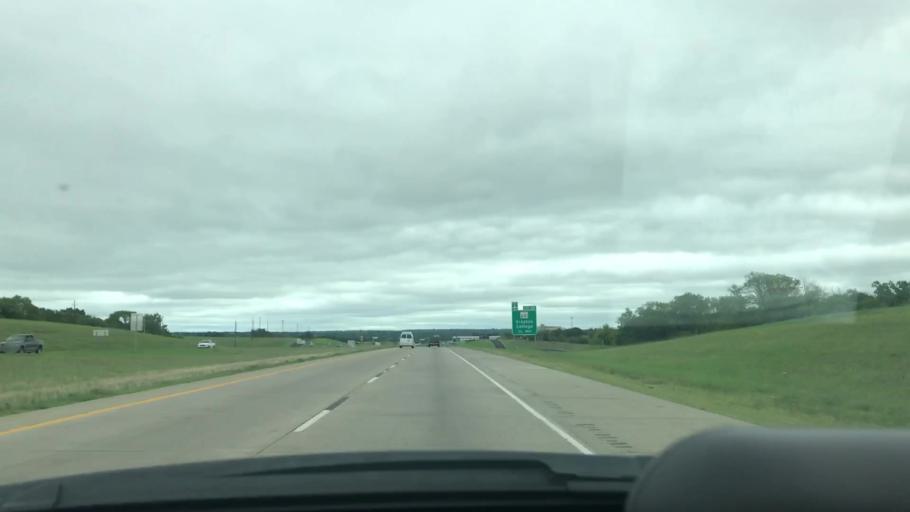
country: US
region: Texas
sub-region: Grayson County
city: Sherman
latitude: 33.6957
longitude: -96.5979
